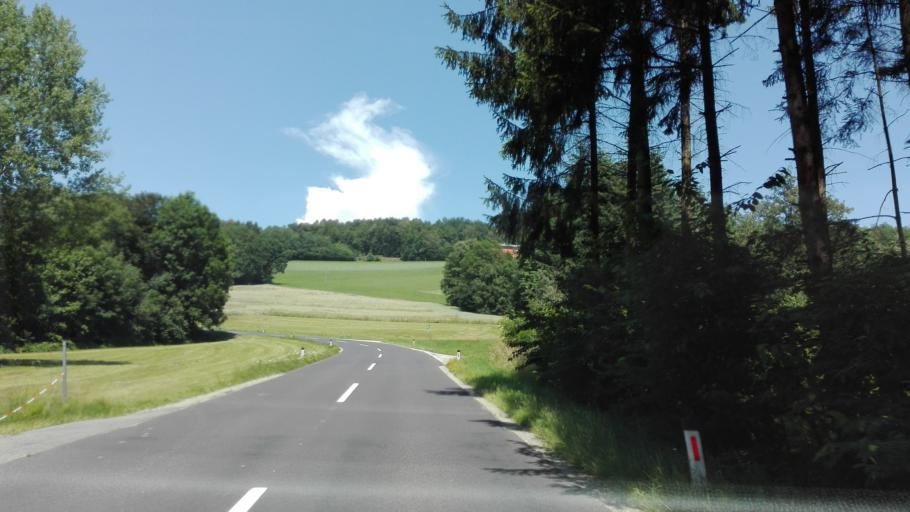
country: AT
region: Upper Austria
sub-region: Politischer Bezirk Grieskirchen
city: Grieskirchen
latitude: 48.3617
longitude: 13.8713
